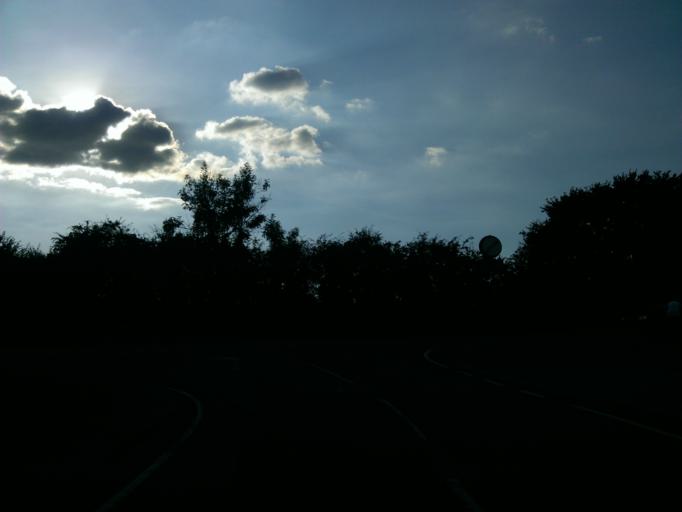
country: GB
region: England
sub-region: Essex
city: Sible Hedingham
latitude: 51.9900
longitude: 0.5852
